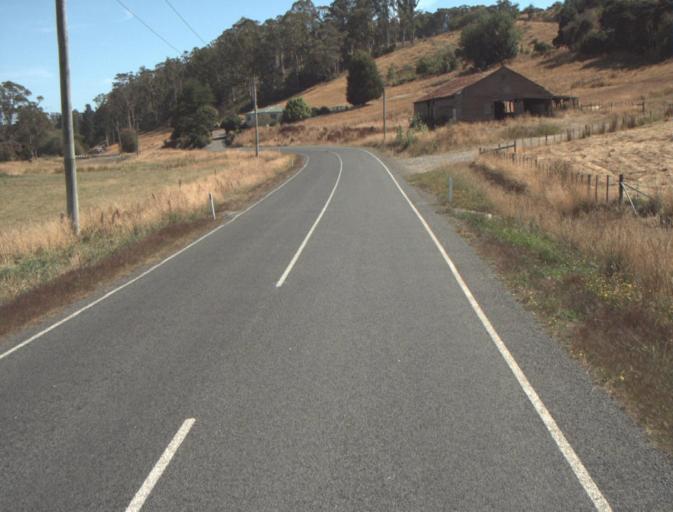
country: AU
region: Tasmania
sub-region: Launceston
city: Mayfield
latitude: -41.2380
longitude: 147.2156
